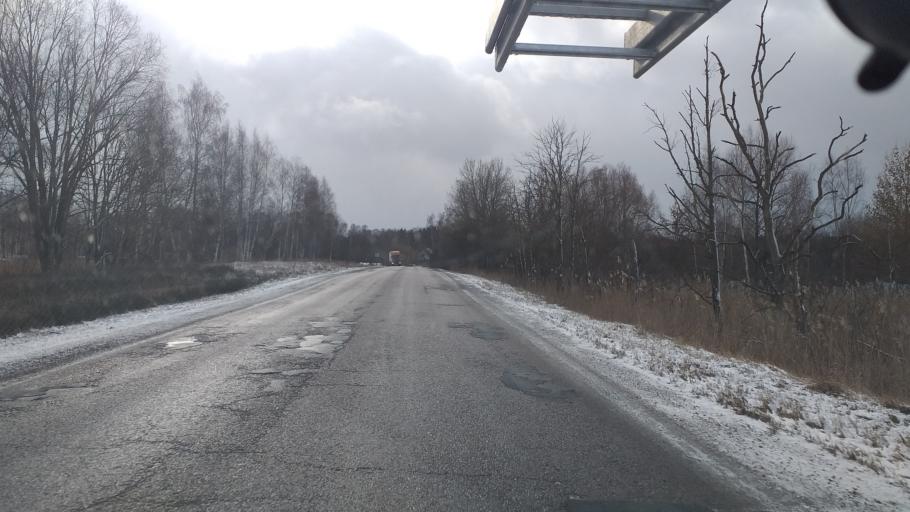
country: LV
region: Riga
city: Bolderaja
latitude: 56.9897
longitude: 24.0316
